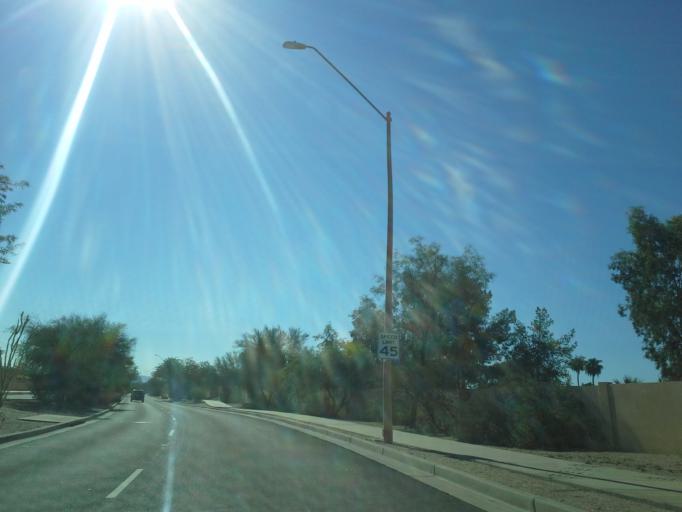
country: US
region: Arizona
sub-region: Maricopa County
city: Scottsdale
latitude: 33.6030
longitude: -111.8536
